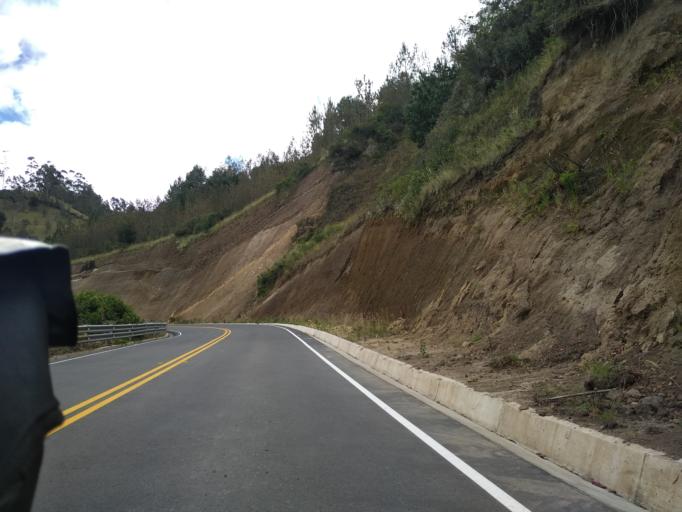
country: EC
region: Cotopaxi
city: Saquisili
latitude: -0.7223
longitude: -78.8919
